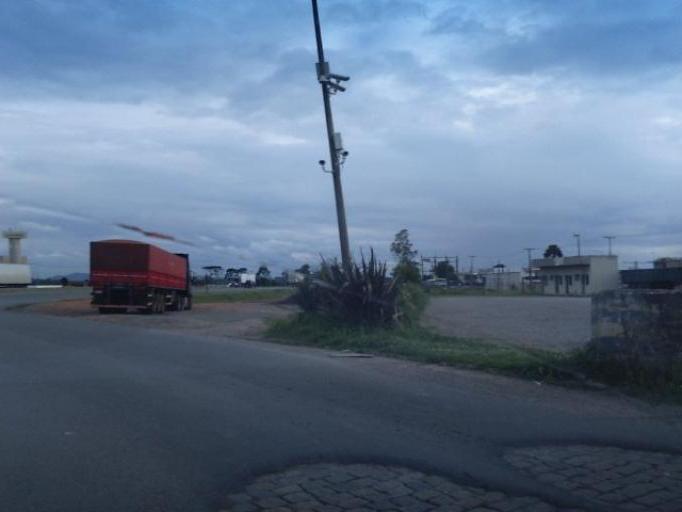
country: BR
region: Parana
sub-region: Sao Jose Dos Pinhais
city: Sao Jose dos Pinhais
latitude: -25.5428
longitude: -49.1513
